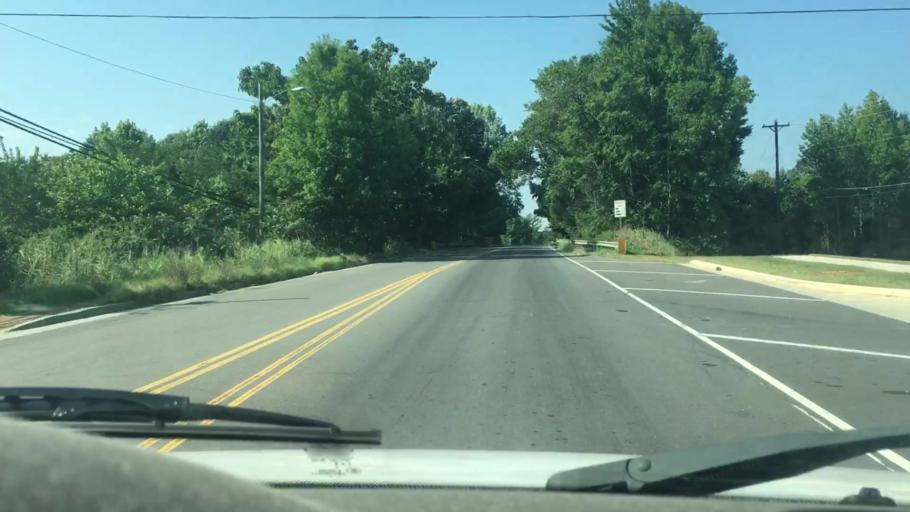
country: US
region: North Carolina
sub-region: Mecklenburg County
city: Charlotte
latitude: 35.2251
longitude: -80.9110
